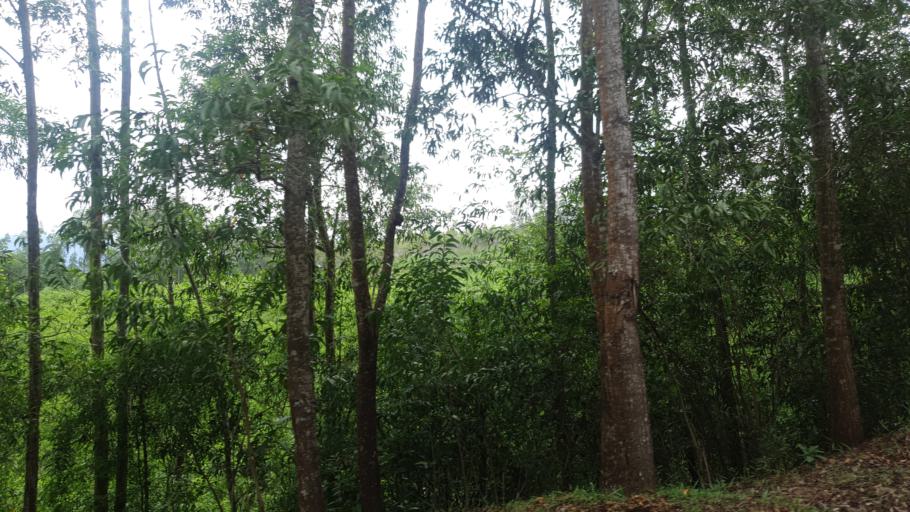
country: IN
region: Kerala
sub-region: Thiruvananthapuram
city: Nedumangad
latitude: 8.6295
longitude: 77.1287
